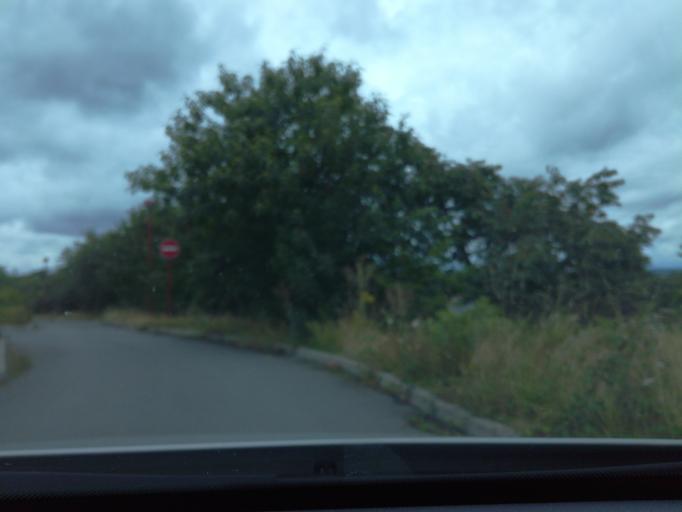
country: FR
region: Brittany
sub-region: Departement d'Ille-et-Vilaine
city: Saint-Aubin-du-Cormier
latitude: 48.2625
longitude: -1.4034
